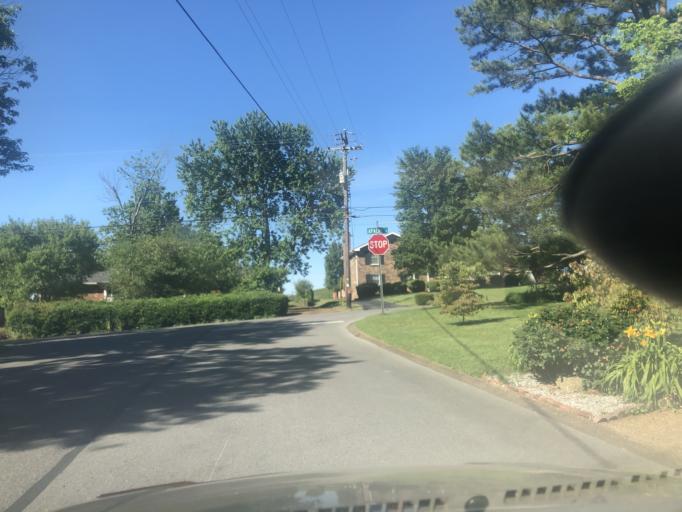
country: US
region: Tennessee
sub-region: Davidson County
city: Lakewood
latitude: 36.2452
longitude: -86.6718
